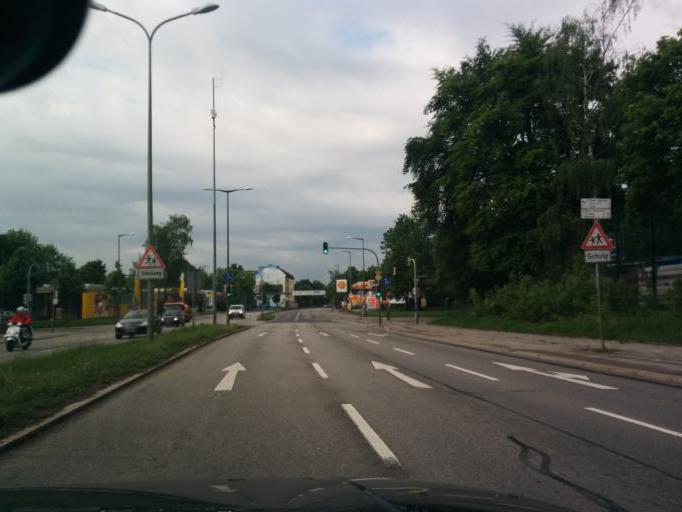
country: DE
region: Bavaria
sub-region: Upper Bavaria
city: Bogenhausen
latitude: 48.1159
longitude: 11.6179
